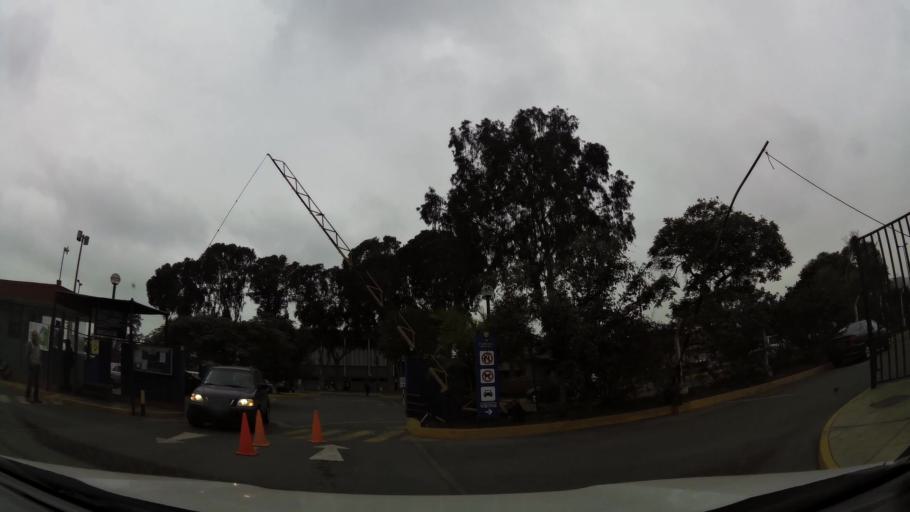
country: PE
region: Lima
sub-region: Lima
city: San Luis
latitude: -12.0983
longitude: -76.9968
